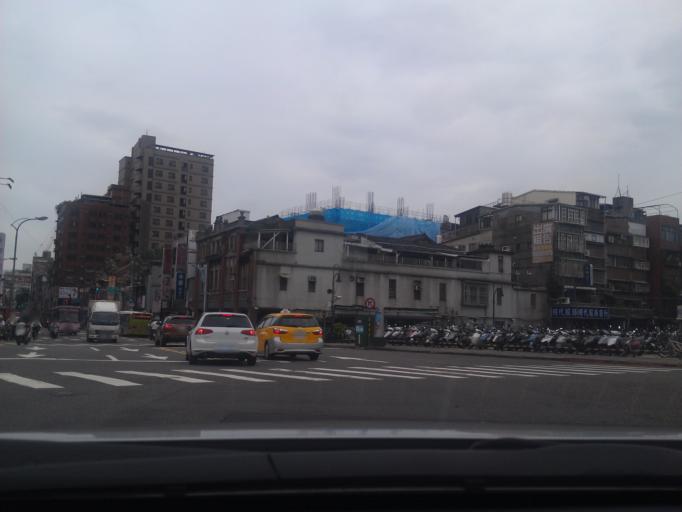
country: TW
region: Taipei
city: Taipei
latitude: 25.0337
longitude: 121.5008
